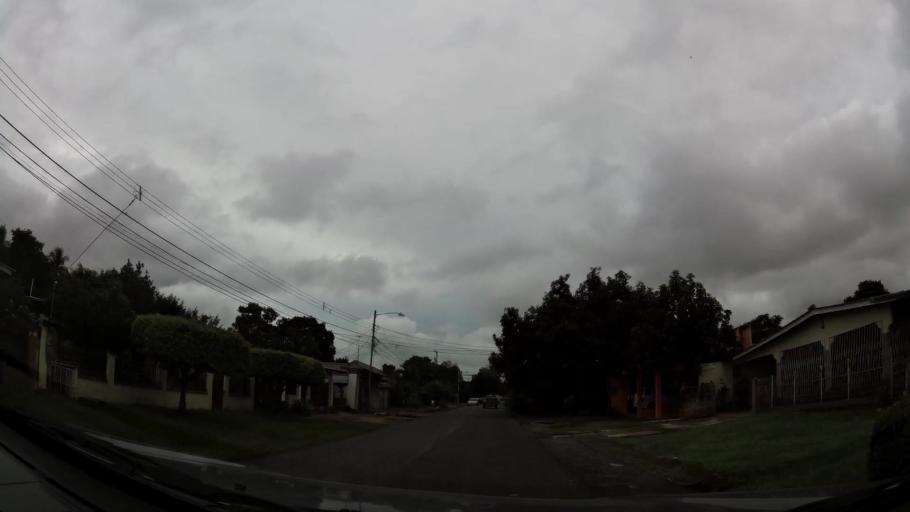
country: PA
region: Chiriqui
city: David
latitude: 8.4260
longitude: -82.4385
